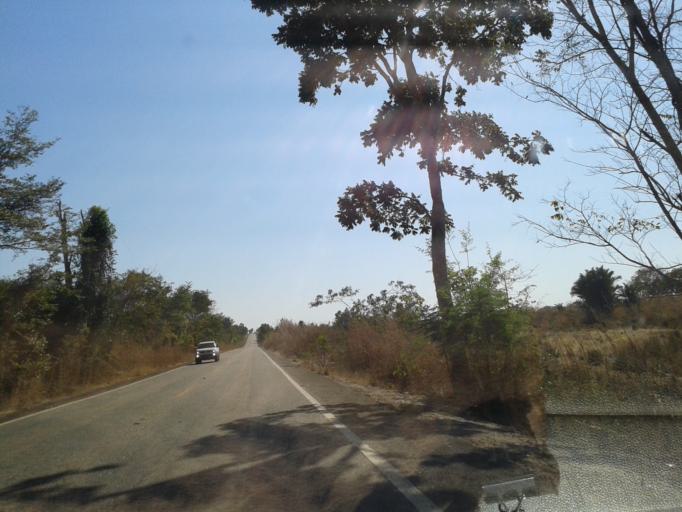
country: BR
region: Goias
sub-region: Mozarlandia
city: Mozarlandia
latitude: -14.5420
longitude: -50.4901
